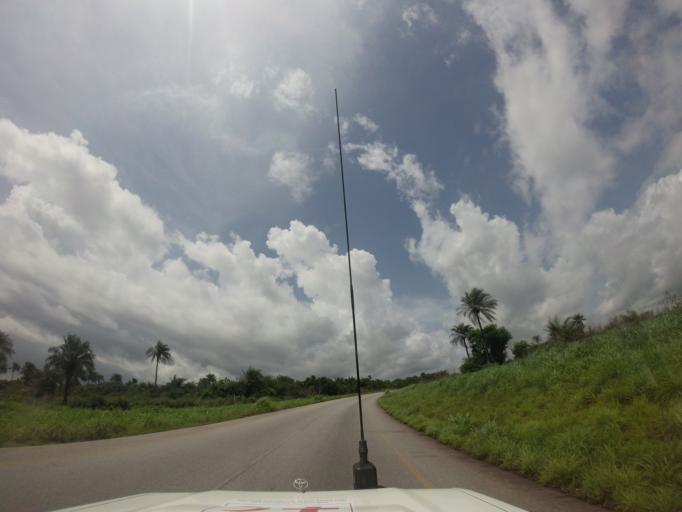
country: SL
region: Northern Province
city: Lunsar
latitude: 8.4855
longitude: -12.6214
